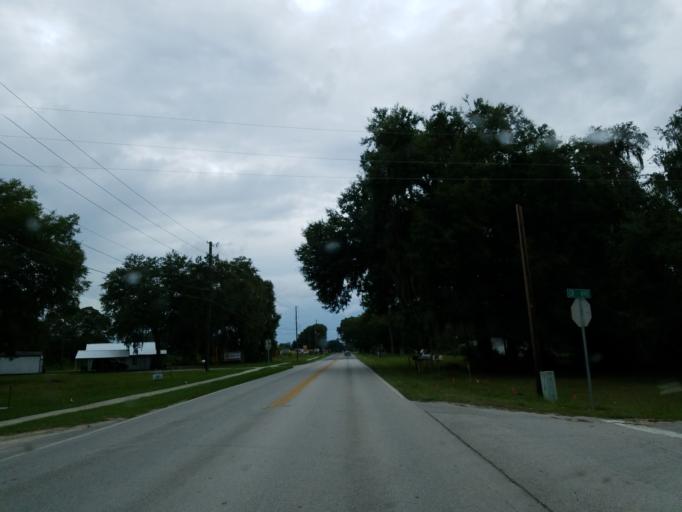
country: US
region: Florida
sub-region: Sumter County
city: Lake Panasoffkee
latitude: 28.7552
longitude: -82.1050
